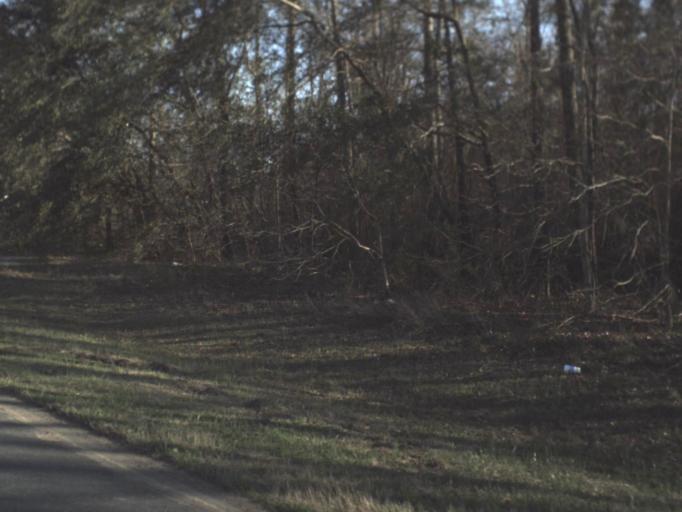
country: US
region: Florida
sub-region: Jackson County
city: Sneads
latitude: 30.7150
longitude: -84.9529
